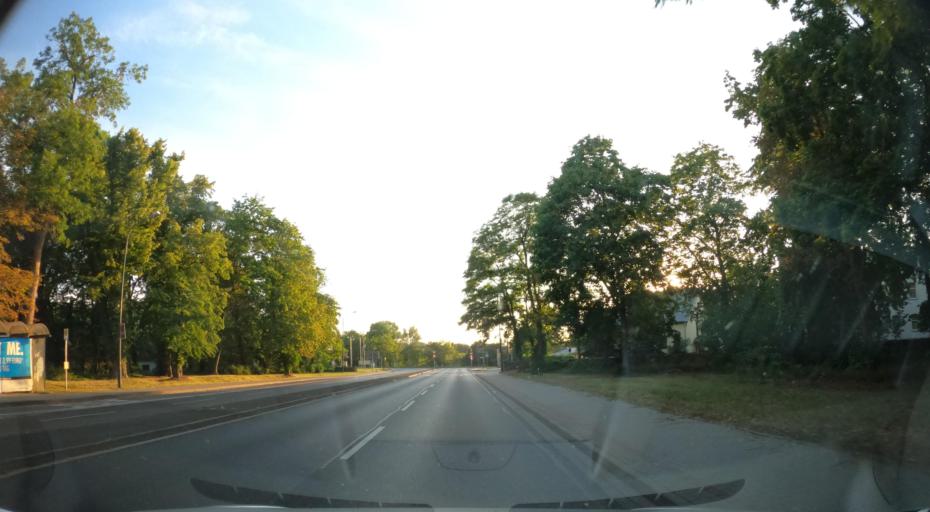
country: DE
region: Mecklenburg-Vorpommern
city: Pasewalk
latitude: 53.4996
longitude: 13.9855
